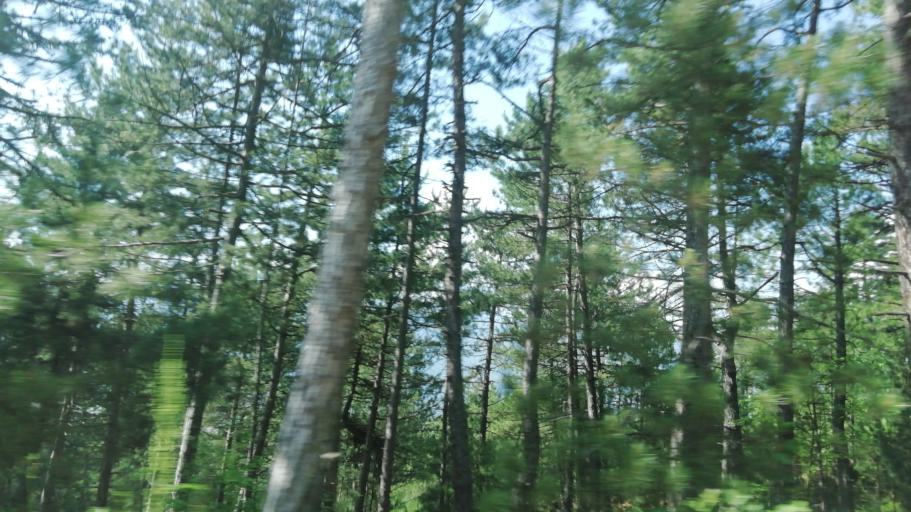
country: TR
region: Karabuk
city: Karabuk
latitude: 41.1243
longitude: 32.5849
